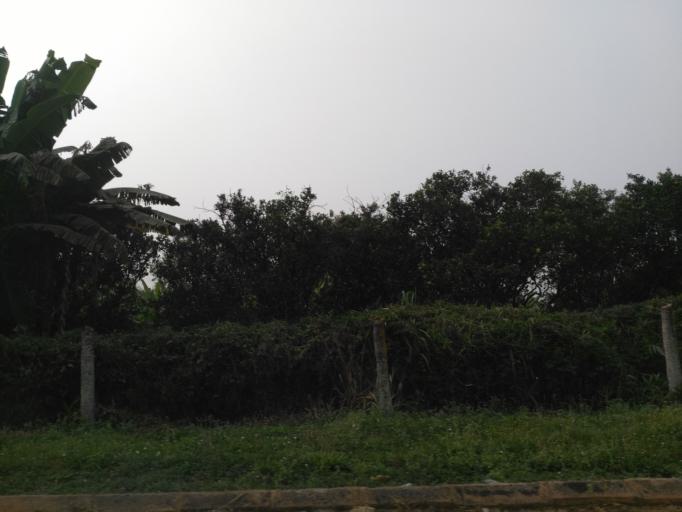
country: GH
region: Ashanti
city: Kumasi
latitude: 6.6514
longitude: -1.6270
